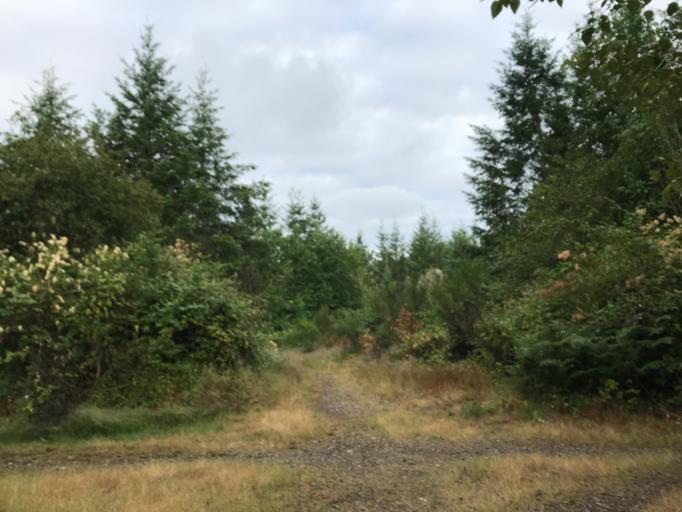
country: US
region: Washington
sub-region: King County
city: Black Diamond
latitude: 47.3360
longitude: -122.0185
